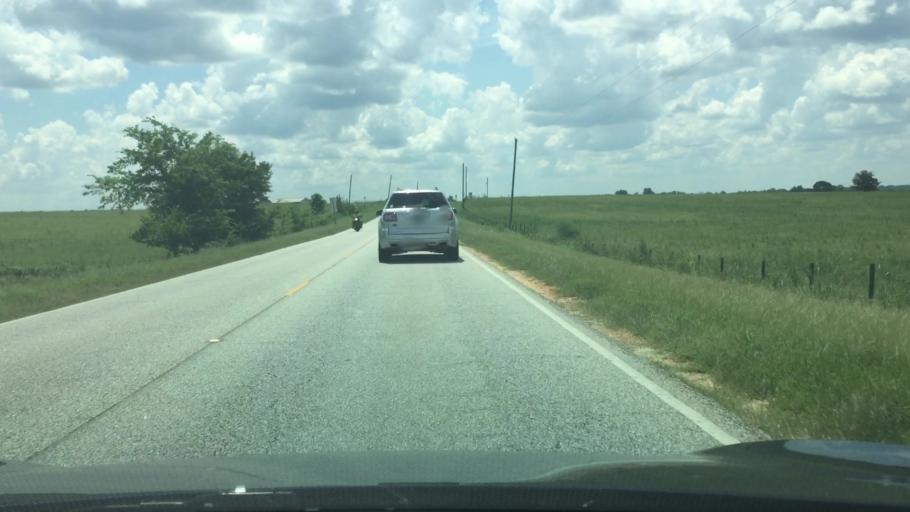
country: US
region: Alabama
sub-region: Montgomery County
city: Pike Road
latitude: 32.2757
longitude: -86.1007
